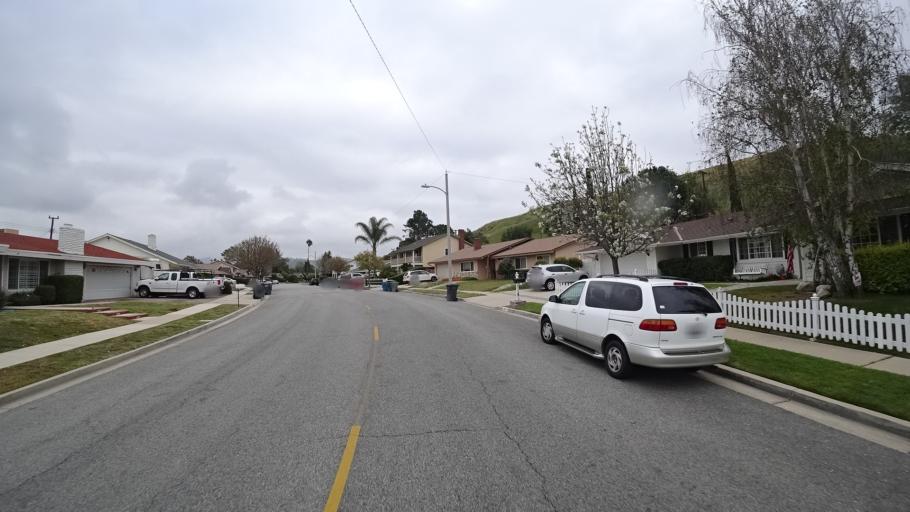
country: US
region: California
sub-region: Ventura County
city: Thousand Oaks
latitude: 34.2038
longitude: -118.8735
